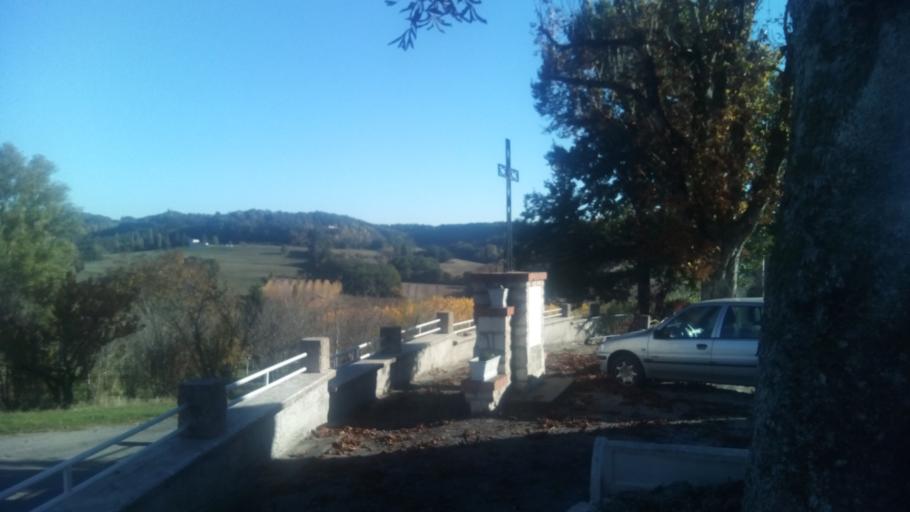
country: FR
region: Midi-Pyrenees
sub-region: Departement du Tarn-et-Garonne
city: Cazes-Mondenard
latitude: 44.2673
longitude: 1.2365
